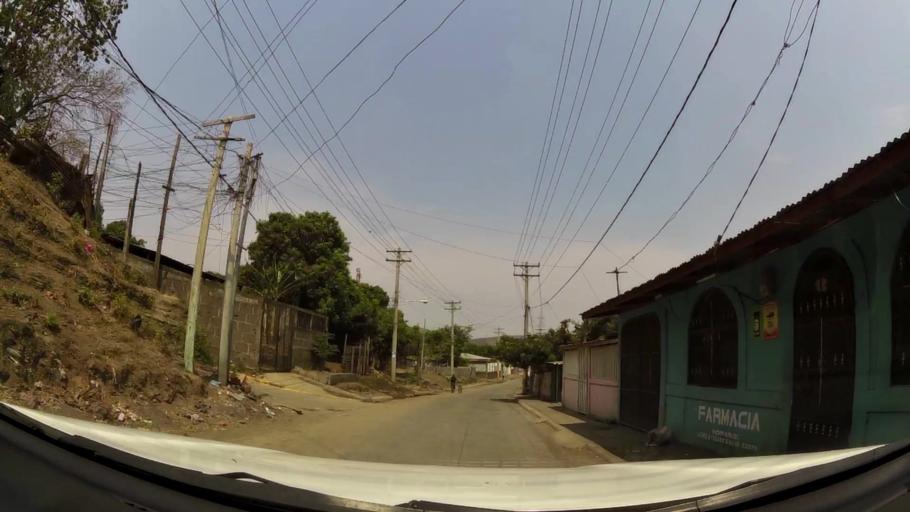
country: NI
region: Managua
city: Ciudad Sandino
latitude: 12.1590
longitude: -86.3090
